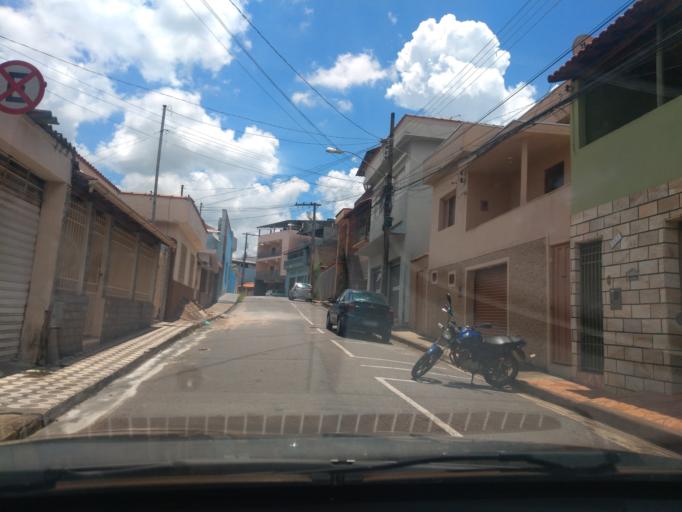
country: BR
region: Minas Gerais
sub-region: Tres Coracoes
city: Tres Coracoes
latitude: -21.6912
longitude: -45.2569
